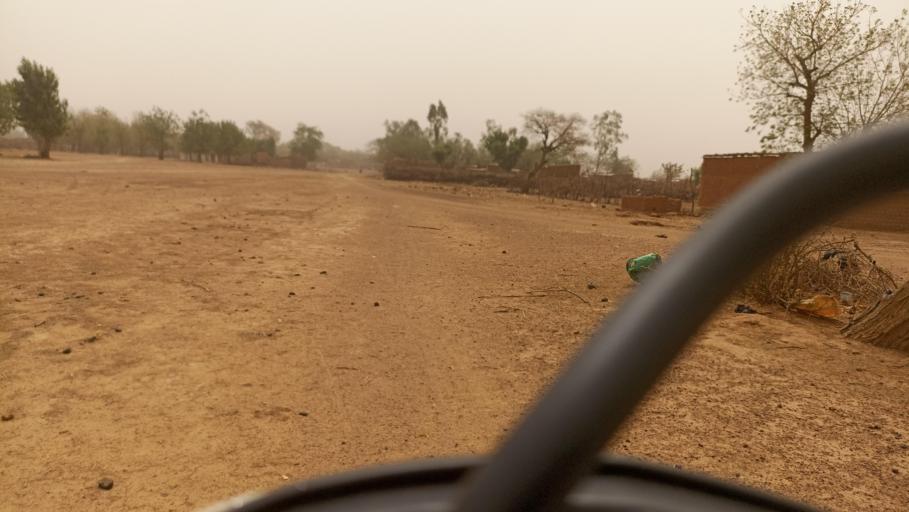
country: BF
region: Nord
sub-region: Province du Zondoma
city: Gourcy
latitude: 13.2484
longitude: -2.5907
